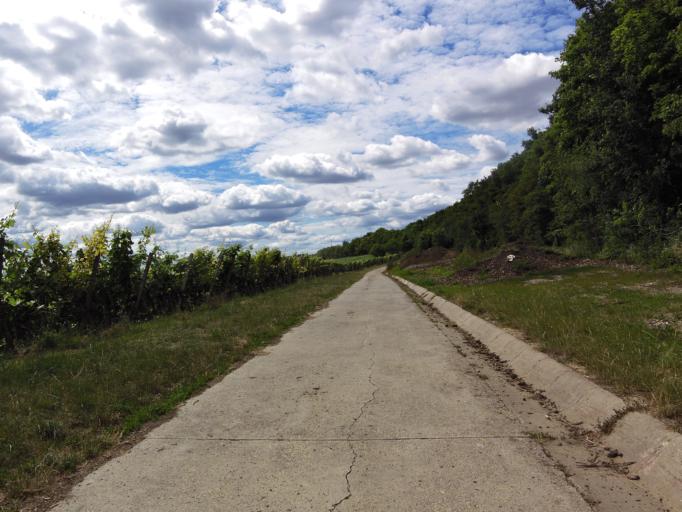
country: DE
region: Bavaria
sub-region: Regierungsbezirk Unterfranken
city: Veitshochheim
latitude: 49.8179
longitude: 9.8911
